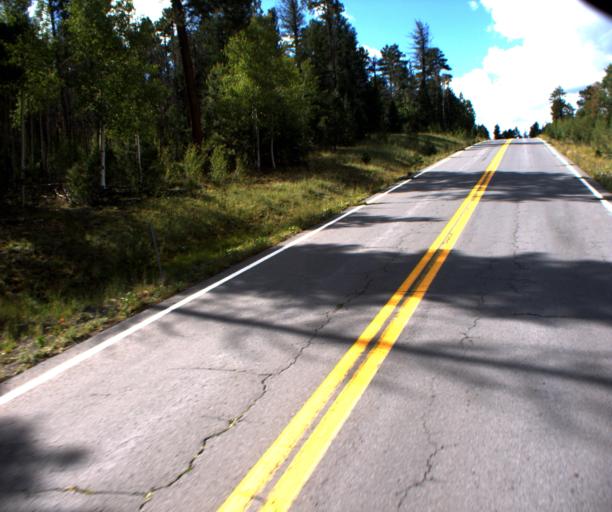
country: US
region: Arizona
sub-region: Apache County
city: Eagar
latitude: 34.0028
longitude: -109.3712
